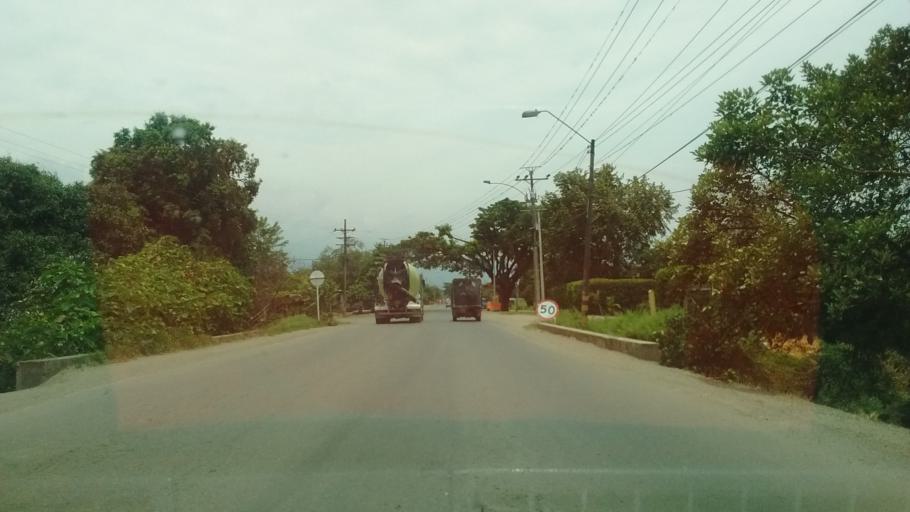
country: CO
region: Valle del Cauca
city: Jamundi
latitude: 3.3165
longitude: -76.4911
